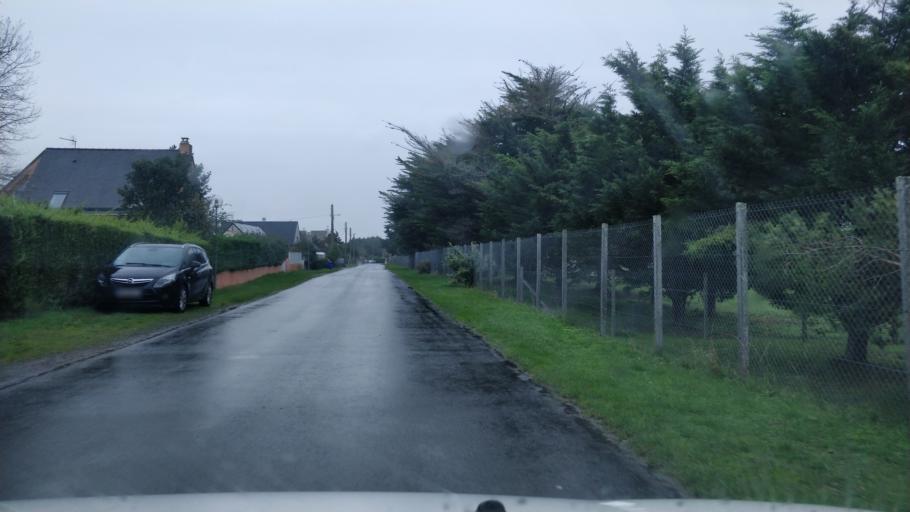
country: FR
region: Lower Normandy
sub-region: Departement de la Manche
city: Brehal
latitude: 48.8999
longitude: -1.5651
